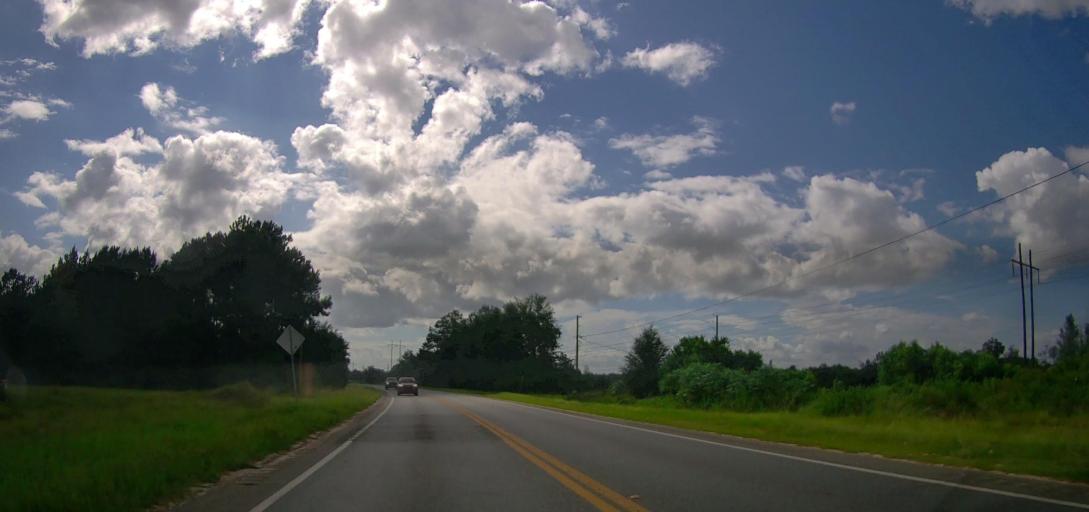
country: US
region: Georgia
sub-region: Coffee County
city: Douglas
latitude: 31.5386
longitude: -82.8121
